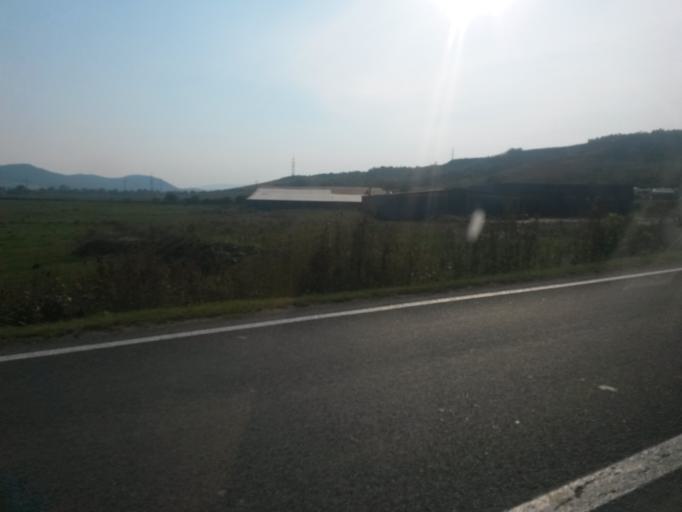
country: RO
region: Alba
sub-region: Comuna Unirea
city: Unirea
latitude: 46.3962
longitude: 23.7984
